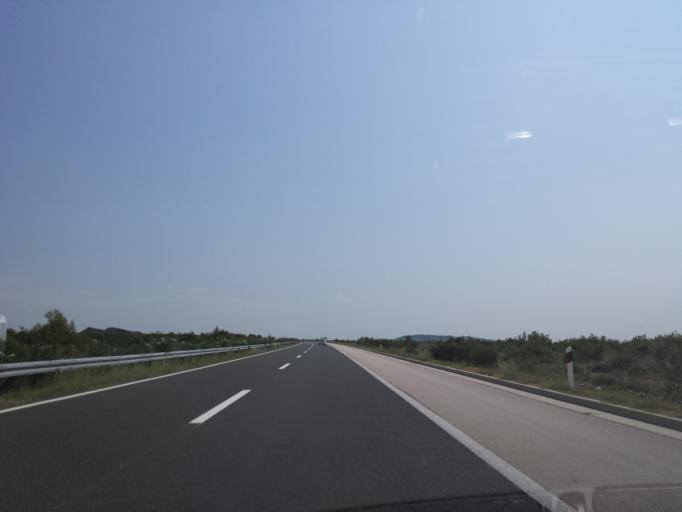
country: HR
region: Zadarska
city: Galovac
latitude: 44.0992
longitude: 15.4698
